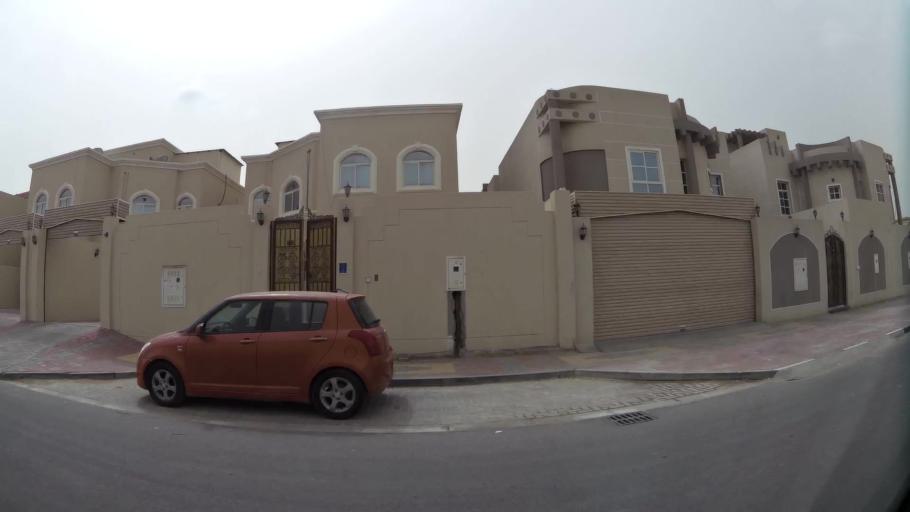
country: QA
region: Baladiyat ad Dawhah
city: Doha
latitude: 25.2322
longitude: 51.5354
